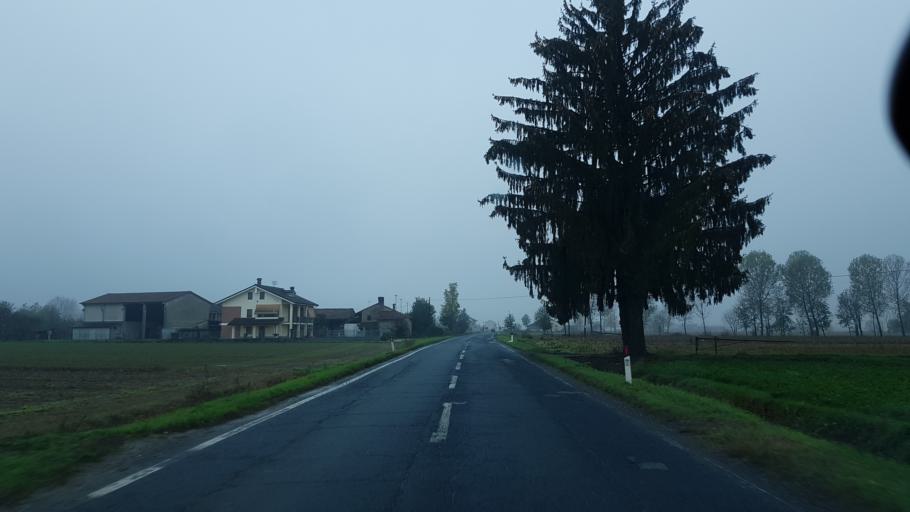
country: IT
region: Piedmont
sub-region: Provincia di Cuneo
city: Genola
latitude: 44.5579
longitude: 7.6453
